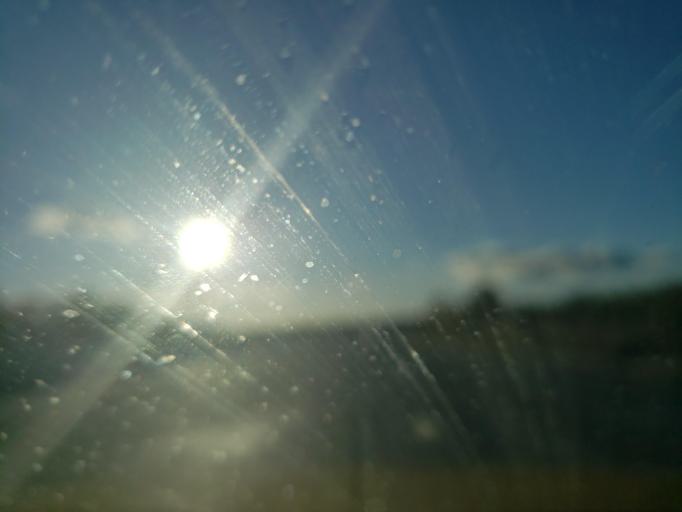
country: ES
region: Castille-La Mancha
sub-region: Province of Toledo
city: Burguillos de Toledo
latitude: 39.8130
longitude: -3.9972
